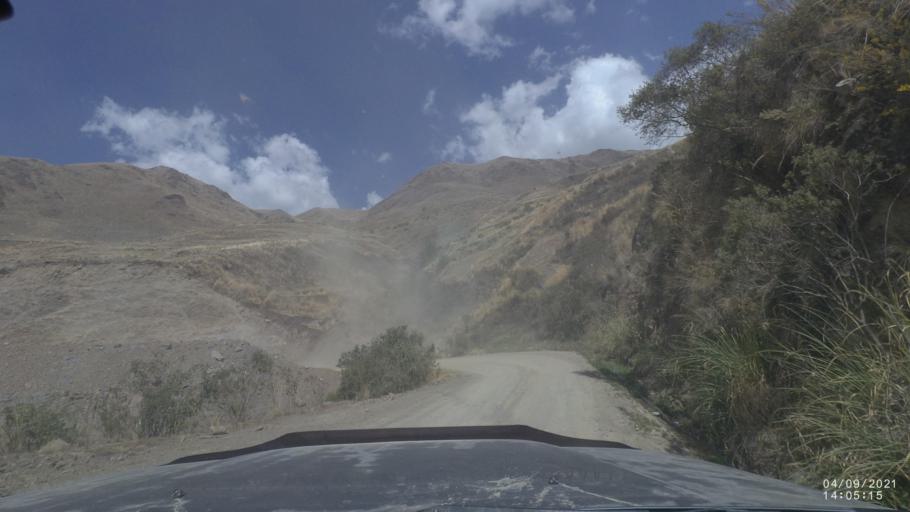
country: BO
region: Cochabamba
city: Sipe Sipe
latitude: -17.2334
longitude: -66.4758
